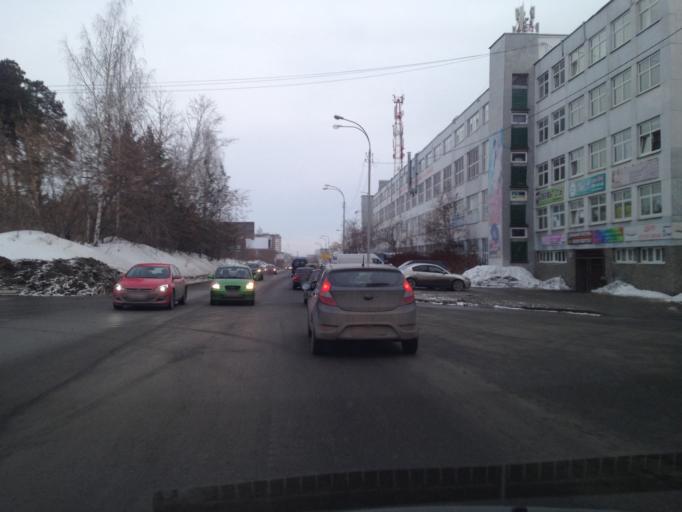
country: RU
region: Sverdlovsk
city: Shirokaya Rechka
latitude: 56.8144
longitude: 60.5351
